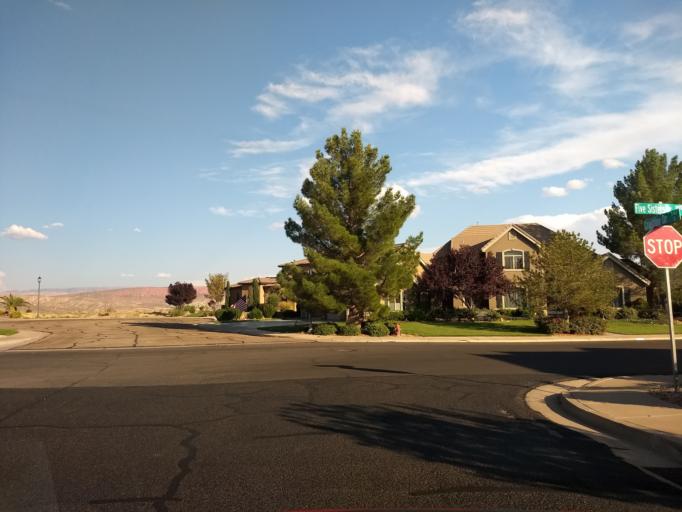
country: US
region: Utah
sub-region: Washington County
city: Saint George
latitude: 37.1025
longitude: -113.5458
